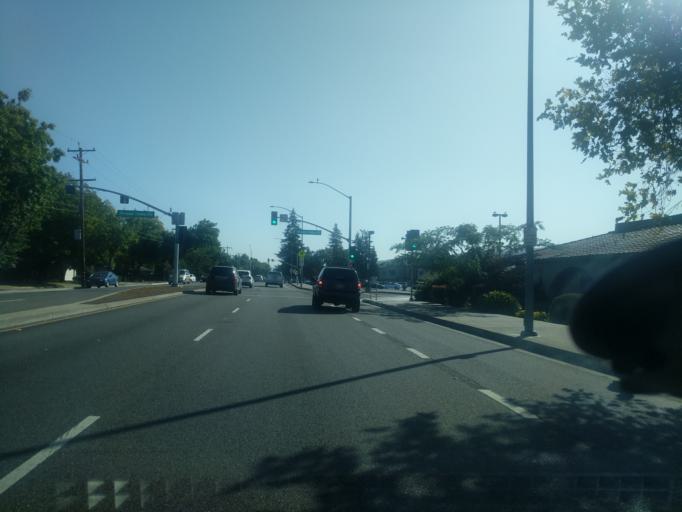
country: US
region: California
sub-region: Alameda County
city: Pleasanton
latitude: 37.6710
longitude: -121.8728
